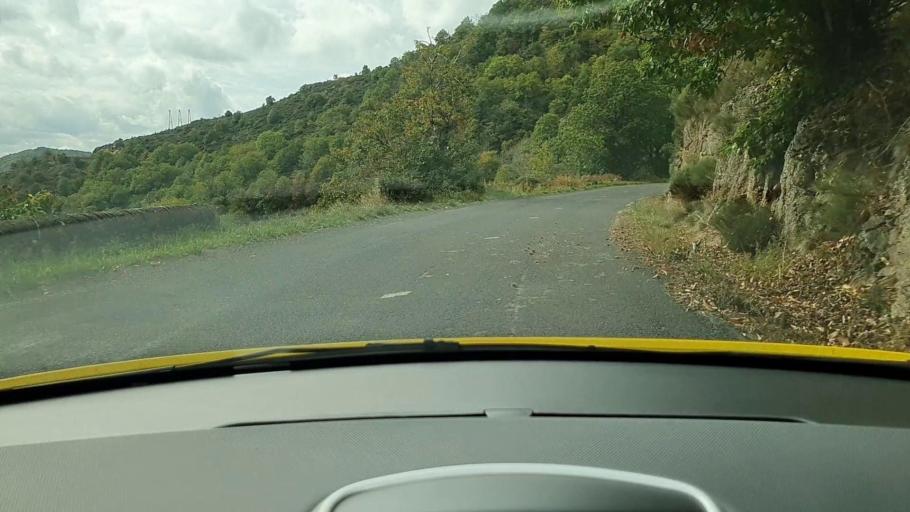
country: FR
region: Languedoc-Roussillon
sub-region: Departement de la Lozere
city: Meyrueis
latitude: 44.0685
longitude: 3.4257
